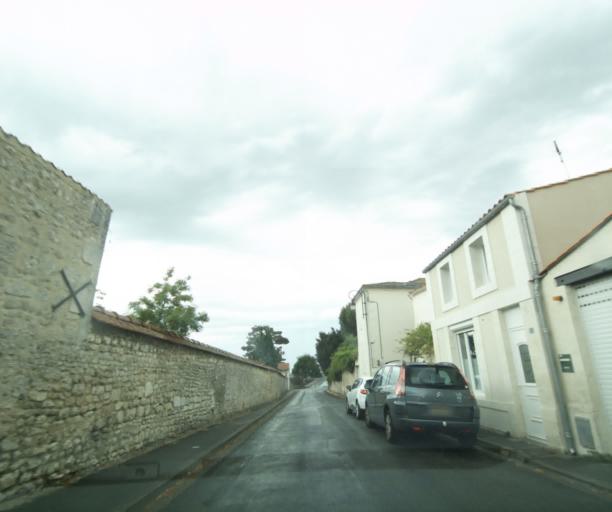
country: FR
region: Poitou-Charentes
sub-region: Departement de la Charente-Maritime
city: Tonnay-Charente
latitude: 45.9424
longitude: -0.8846
